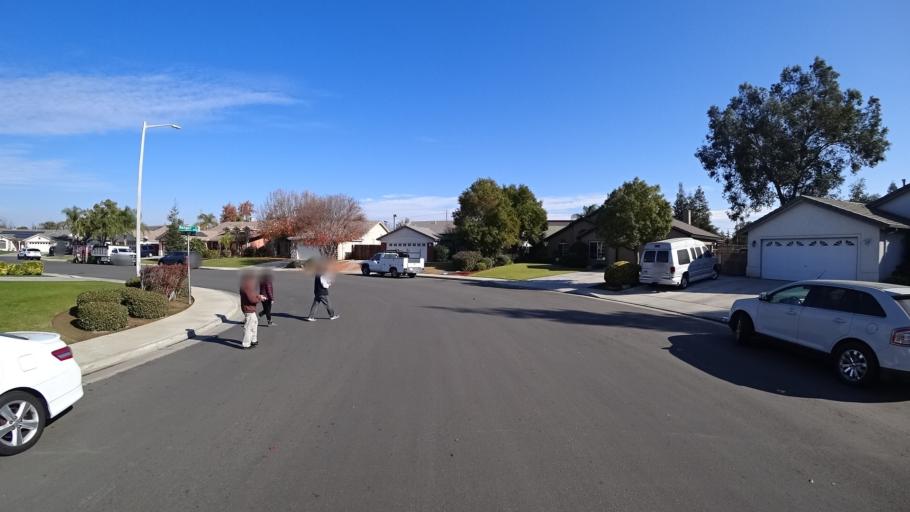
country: US
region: California
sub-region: Kern County
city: Greenacres
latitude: 35.4020
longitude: -119.0948
